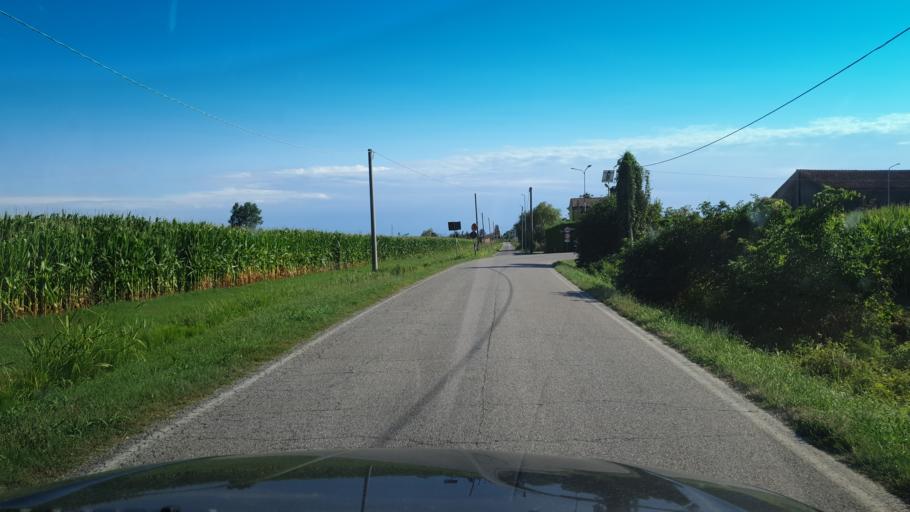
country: IT
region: Veneto
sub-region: Provincia di Rovigo
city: Costa di Rovigo
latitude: 45.0416
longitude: 11.6716
